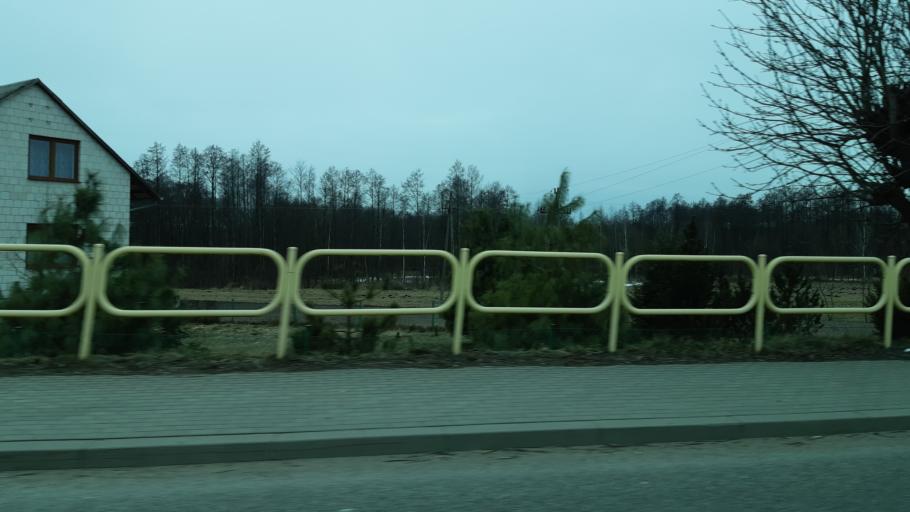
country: PL
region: Podlasie
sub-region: Suwalki
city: Suwalki
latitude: 54.3210
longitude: 22.9677
